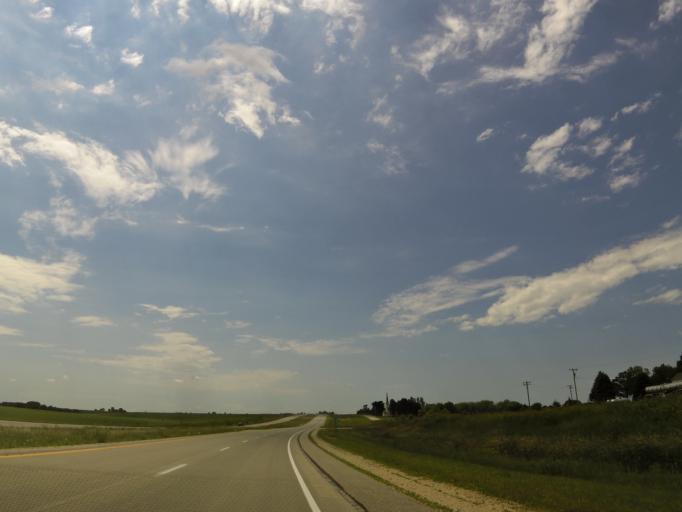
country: US
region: Iowa
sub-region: Bremer County
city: Denver
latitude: 42.7609
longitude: -92.3365
